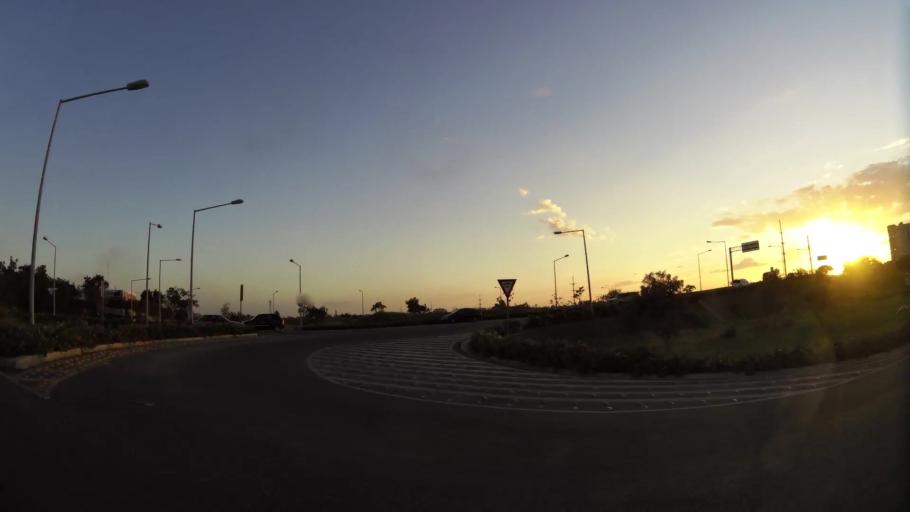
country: DO
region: Santo Domingo
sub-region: Santo Domingo
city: Santo Domingo Este
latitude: 18.4835
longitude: -69.8255
